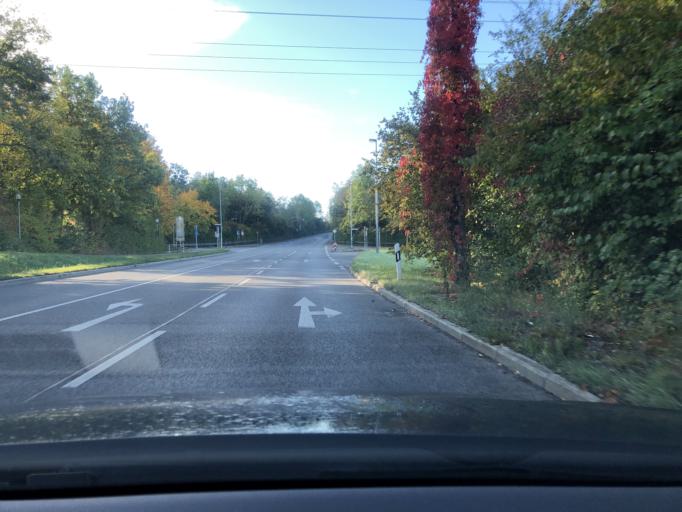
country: DE
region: Baden-Wuerttemberg
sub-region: Regierungsbezirk Stuttgart
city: Magstadt
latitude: 48.7151
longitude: 8.9820
